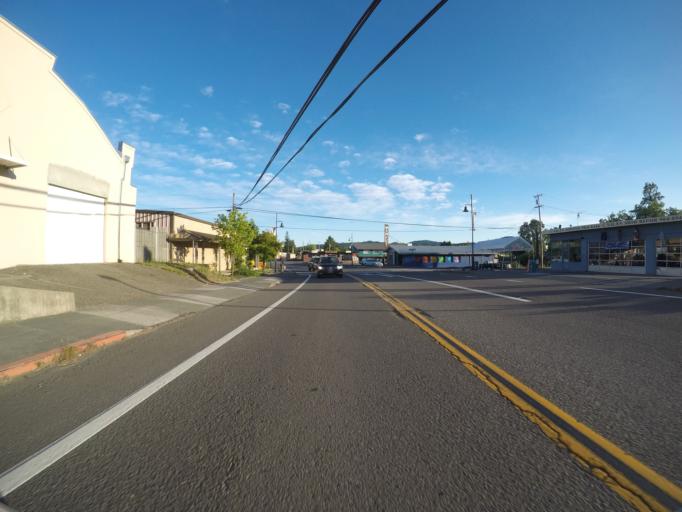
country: US
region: California
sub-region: Mendocino County
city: Laytonville
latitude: 39.6882
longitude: -123.4831
